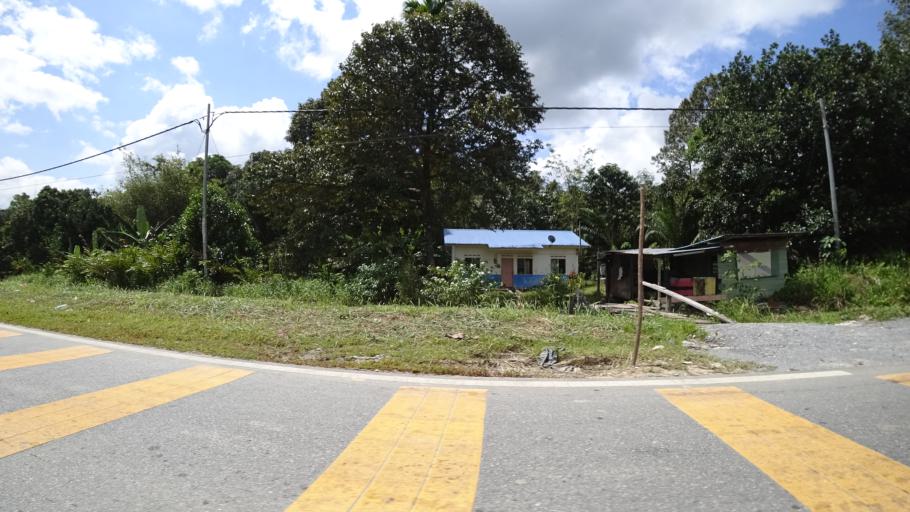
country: MY
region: Sarawak
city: Limbang
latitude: 4.6583
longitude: 114.9548
